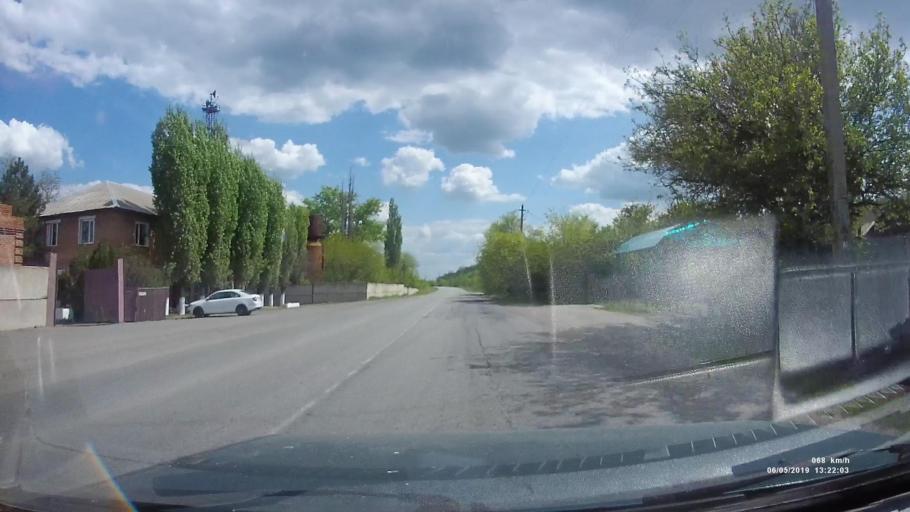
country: RU
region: Rostov
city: Ust'-Donetskiy
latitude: 47.6993
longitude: 40.9155
